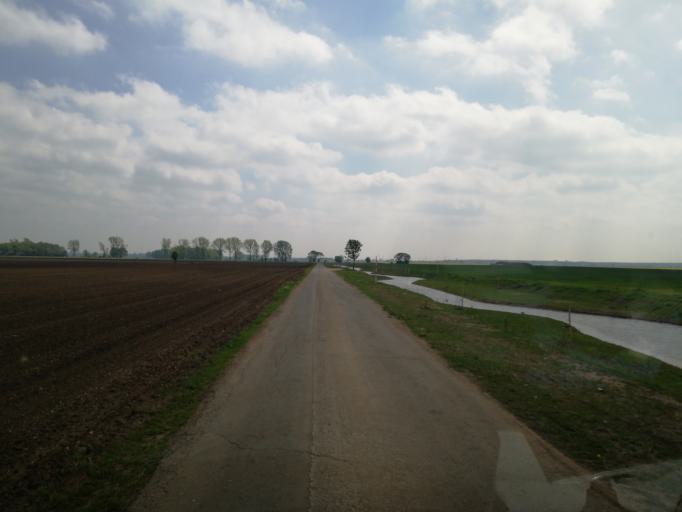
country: DE
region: Brandenburg
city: Doberlug-Kirchhain
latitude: 51.6824
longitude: 13.5344
